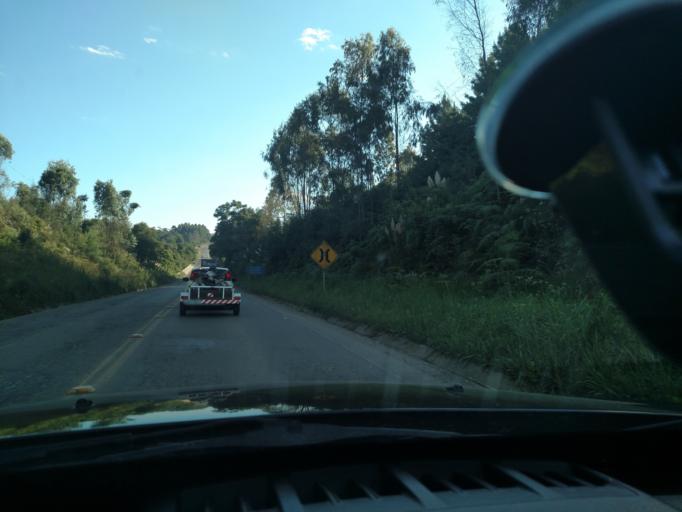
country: BR
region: Santa Catarina
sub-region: Otacilio Costa
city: Otacilio Costa
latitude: -27.5136
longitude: -50.1318
